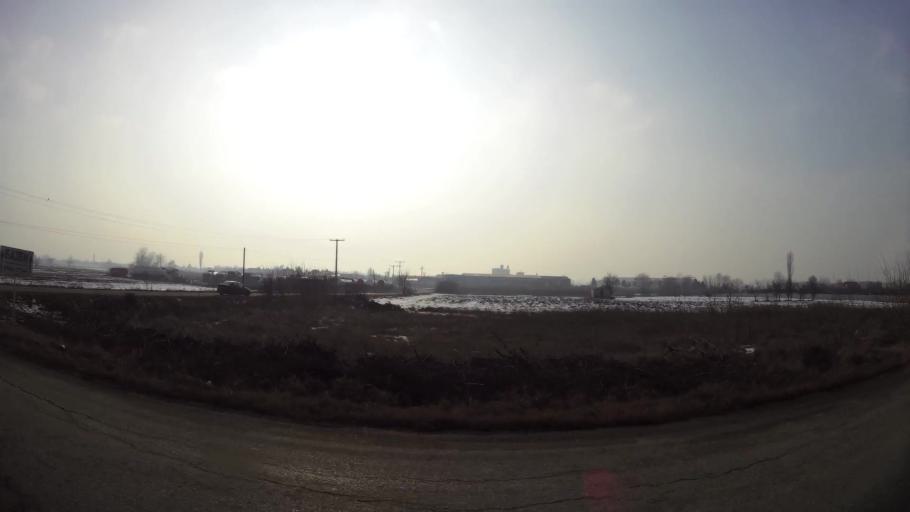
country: MK
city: Kadino
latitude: 41.9776
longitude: 21.6004
